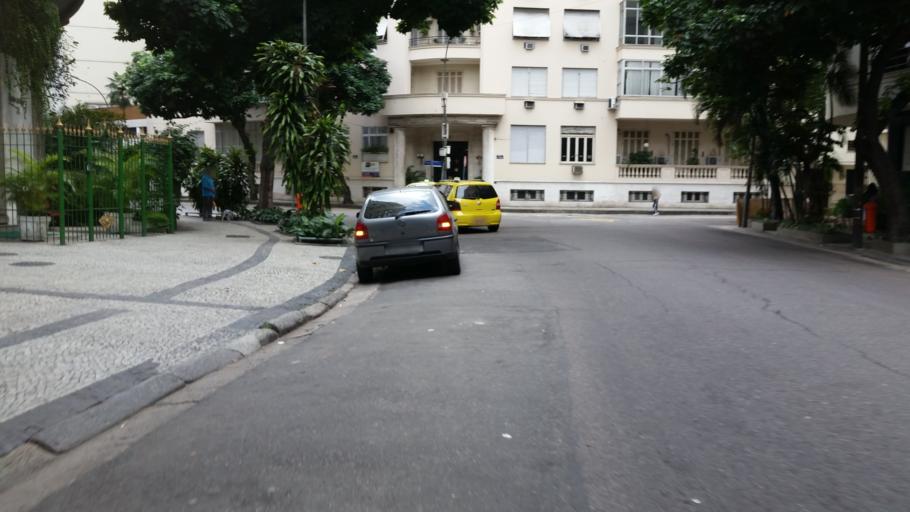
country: BR
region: Rio de Janeiro
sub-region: Rio De Janeiro
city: Rio de Janeiro
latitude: -22.9353
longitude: -43.1753
